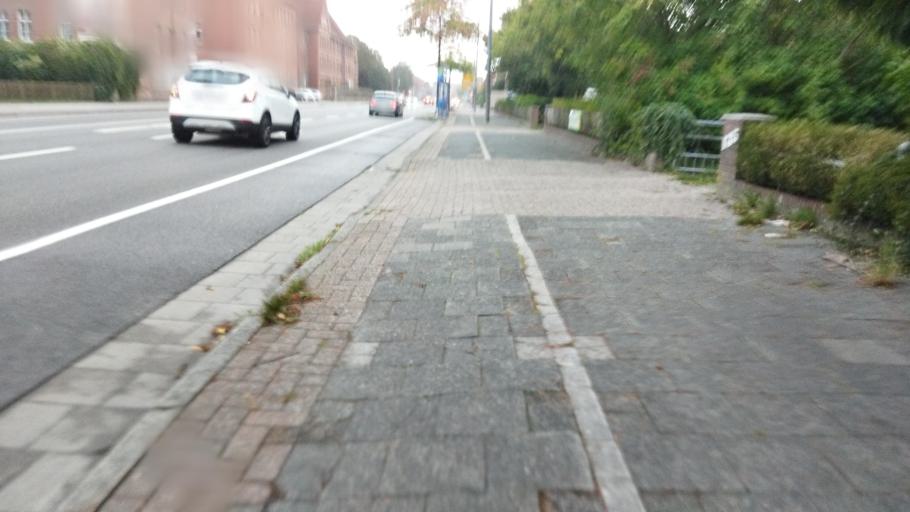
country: DE
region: Lower Saxony
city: Emden
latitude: 53.3830
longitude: 7.2072
